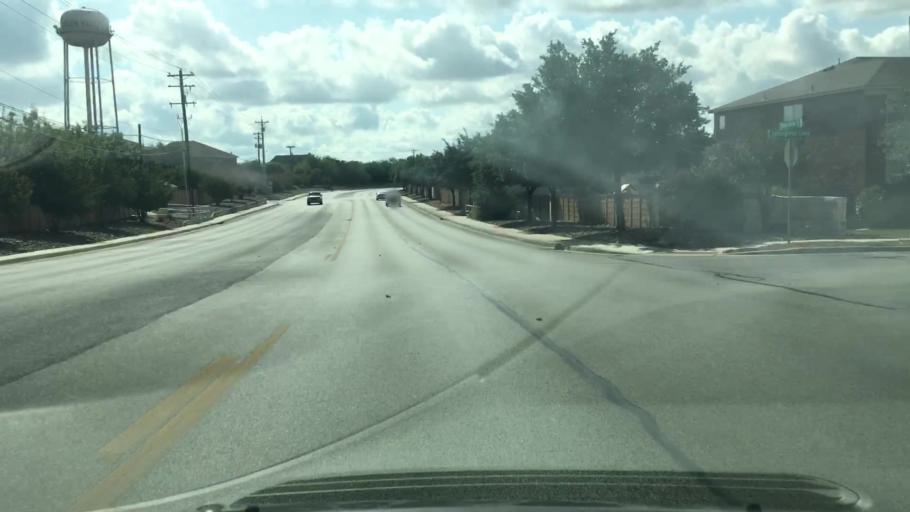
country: US
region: Texas
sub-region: Guadalupe County
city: Northcliff
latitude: 29.5981
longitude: -98.2586
